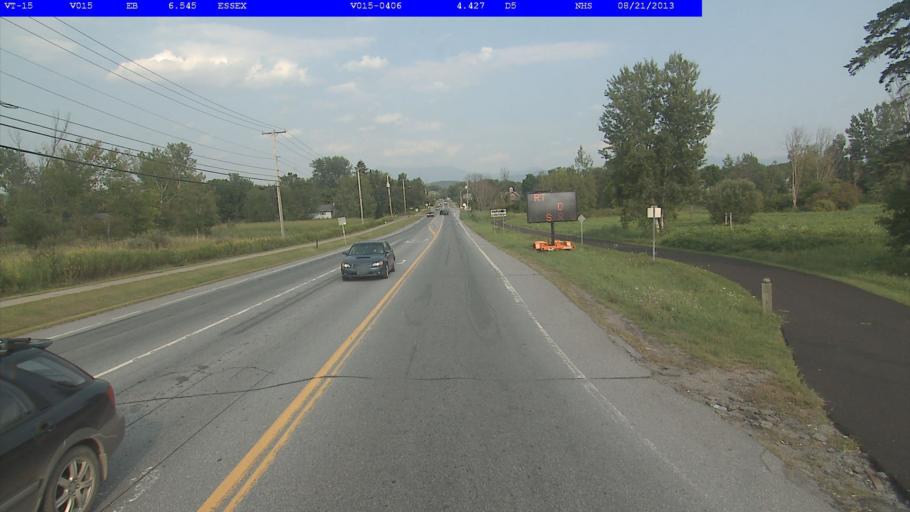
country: US
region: Vermont
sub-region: Chittenden County
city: Essex Junction
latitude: 44.5103
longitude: -73.0781
